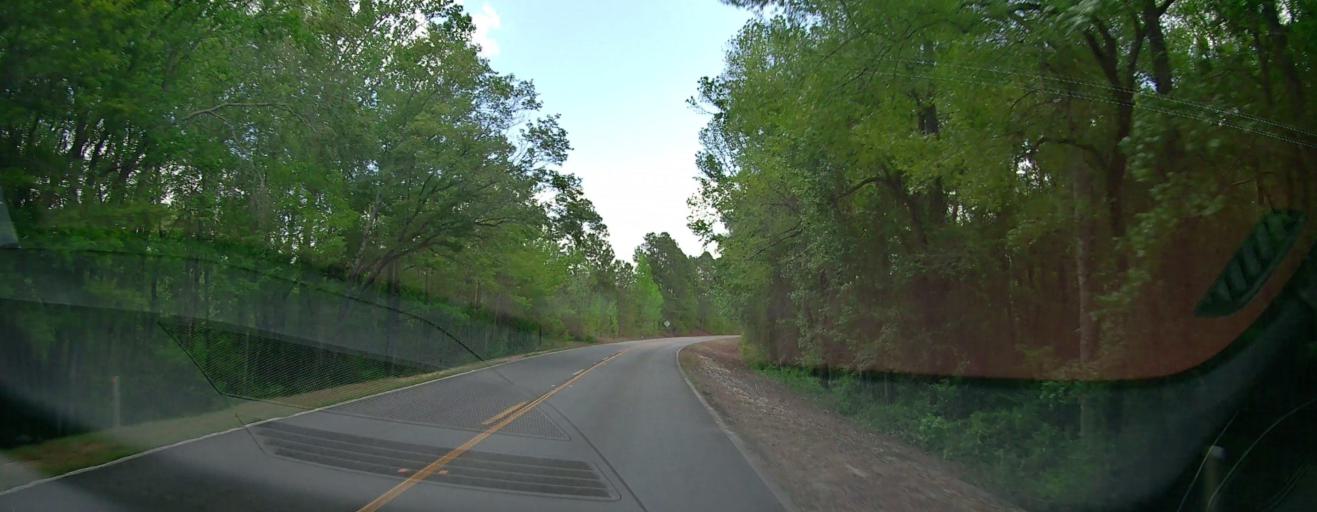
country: US
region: Georgia
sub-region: Treutlen County
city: Soperton
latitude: 32.5238
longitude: -82.6747
